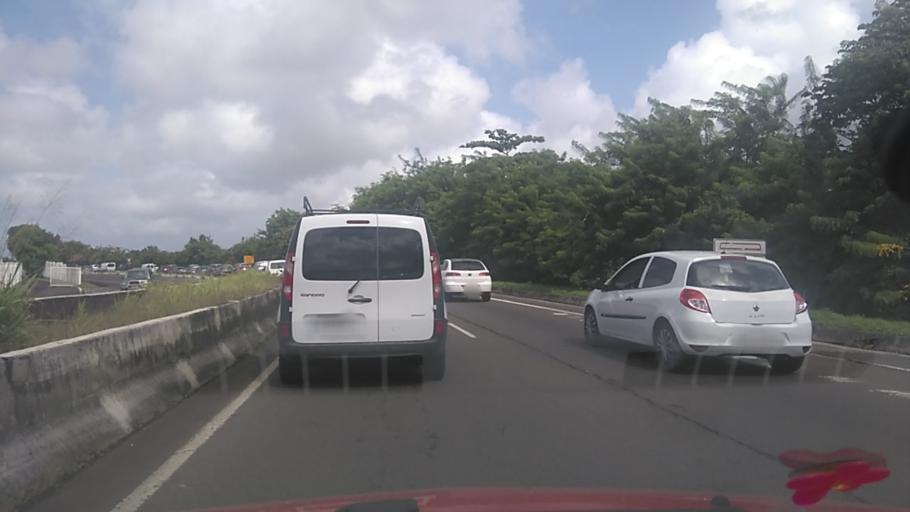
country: MQ
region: Martinique
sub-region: Martinique
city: Le Lamentin
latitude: 14.6252
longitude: -60.9859
